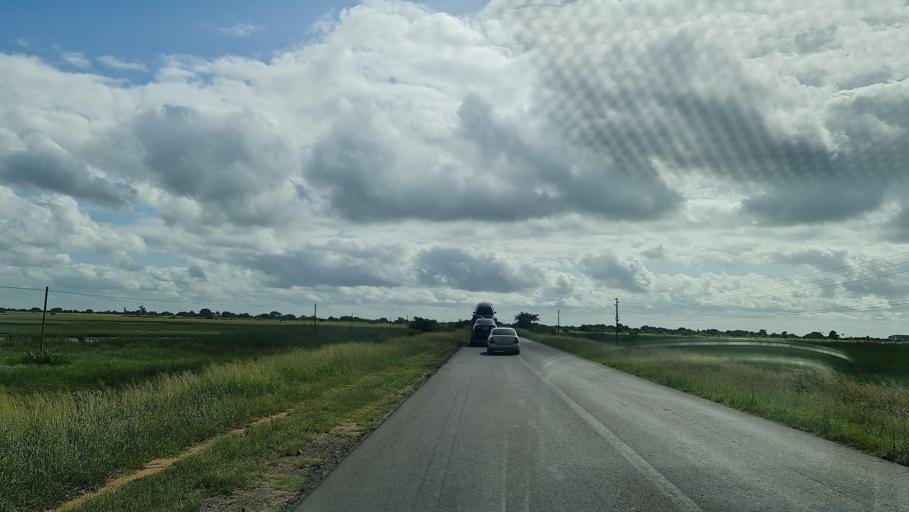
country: MZ
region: Gaza
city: Macia
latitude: -25.0955
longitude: 32.8318
